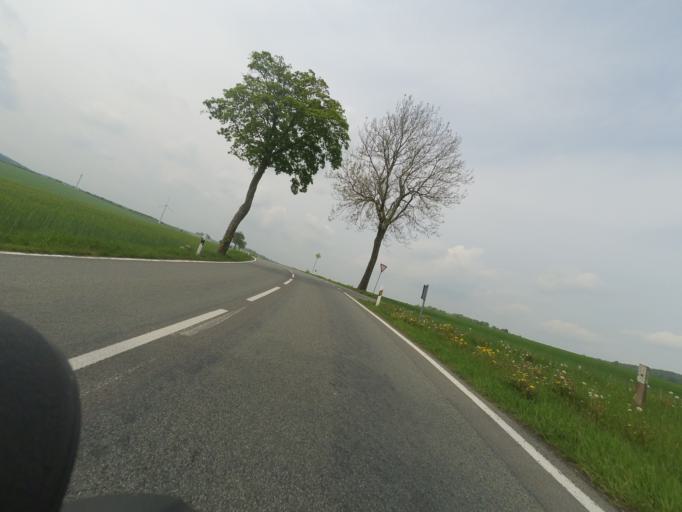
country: DE
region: Saxony
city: Zoblitz
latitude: 50.6505
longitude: 13.2780
